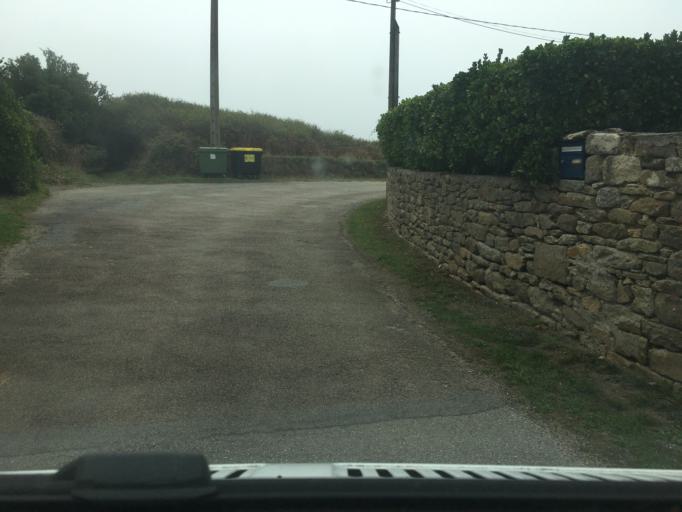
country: FR
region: Brittany
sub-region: Departement du Finistere
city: Plogoff
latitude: 48.0359
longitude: -4.6939
